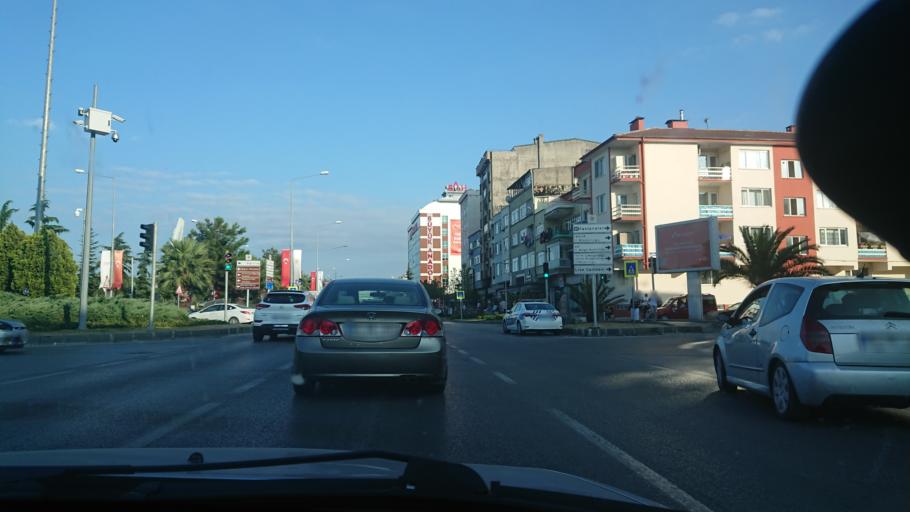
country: TR
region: Samsun
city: Samsun
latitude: 41.2857
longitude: 36.3413
